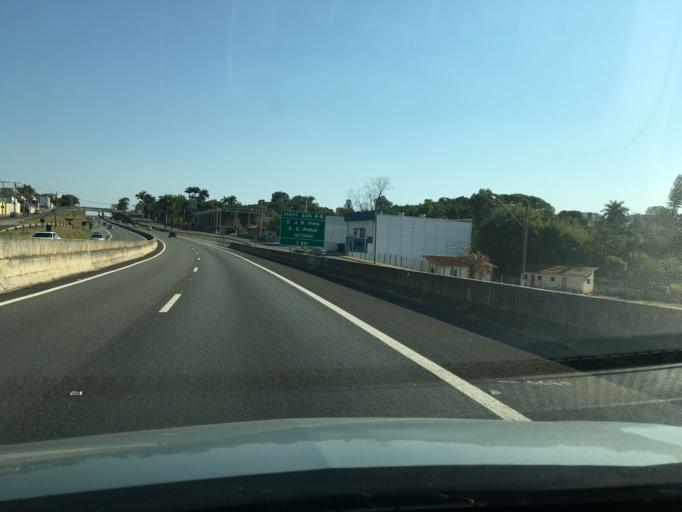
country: BR
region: Sao Paulo
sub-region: Sao Joao Da Boa Vista
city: Sao Joao da Boa Vista
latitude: -21.9809
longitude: -46.7857
